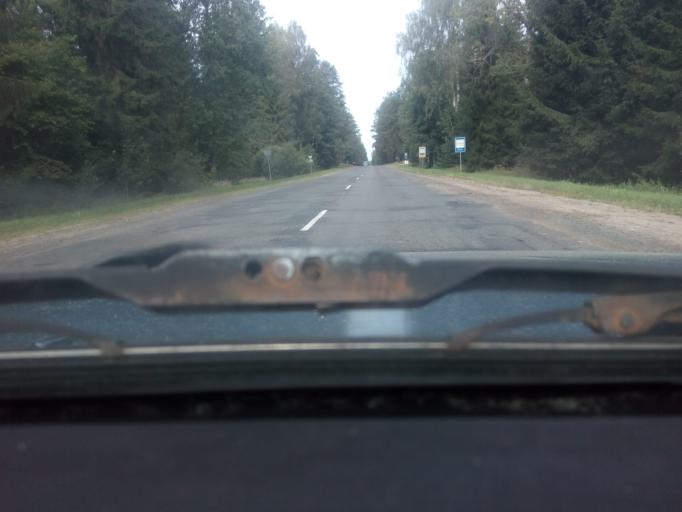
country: BY
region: Vitebsk
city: Vyerkhnyadzvinsk
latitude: 55.7927
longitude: 27.9696
